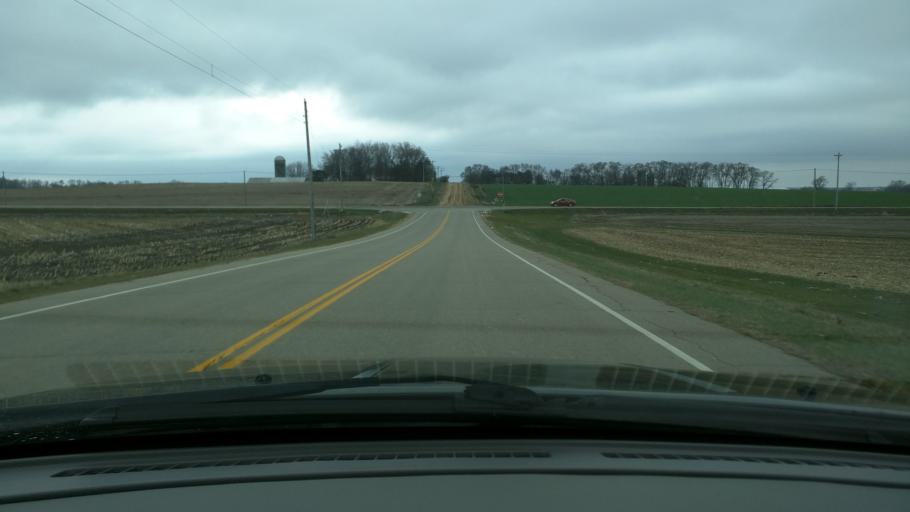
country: US
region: Minnesota
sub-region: Washington County
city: Cottage Grove
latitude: 44.7579
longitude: -92.9239
